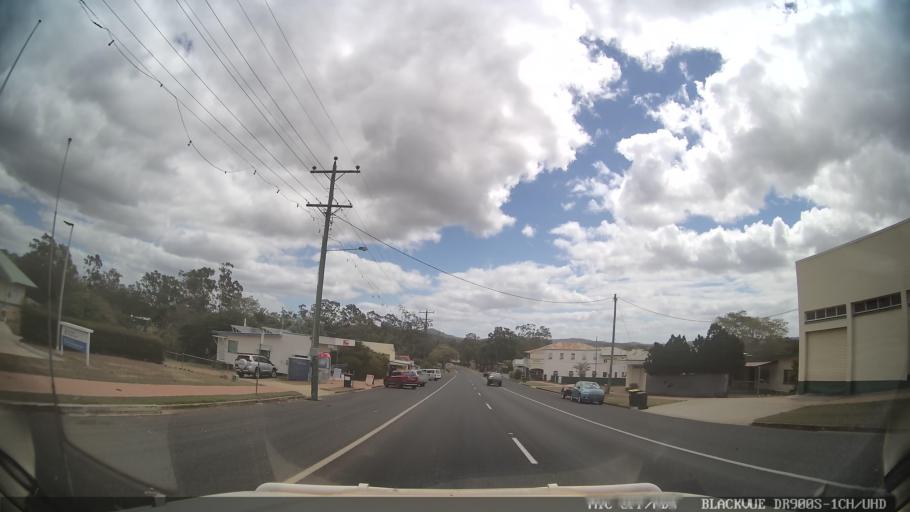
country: AU
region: Queensland
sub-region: Tablelands
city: Ravenshoe
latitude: -17.6767
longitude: 145.1156
